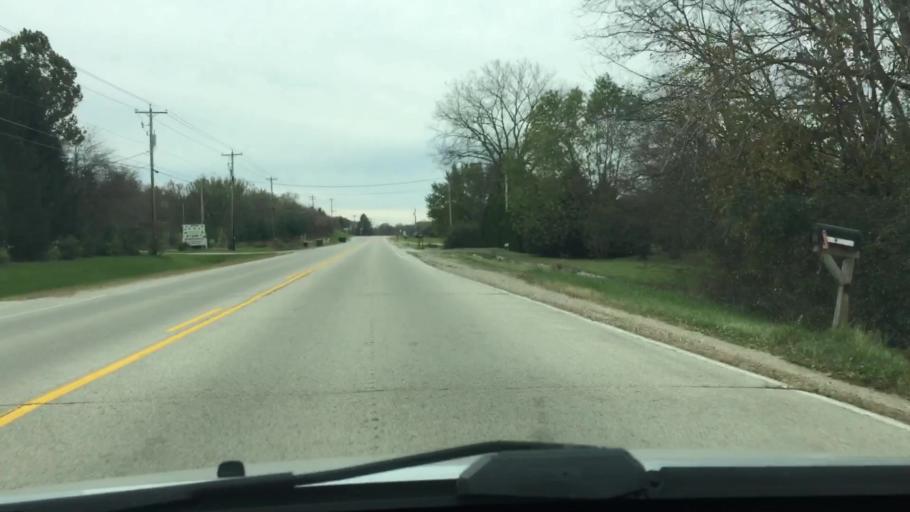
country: US
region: Wisconsin
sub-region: Waukesha County
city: Mukwonago
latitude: 42.8952
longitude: -88.2744
